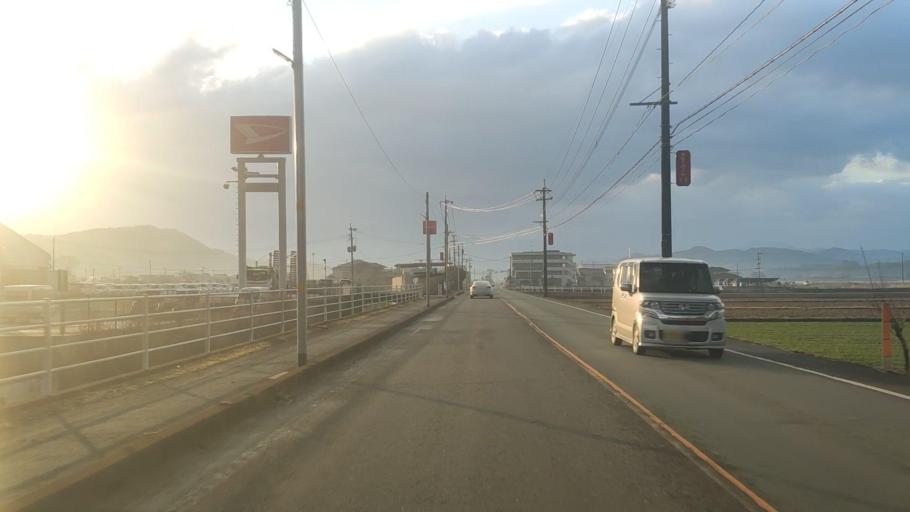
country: JP
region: Kumamoto
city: Uto
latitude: 32.7152
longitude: 130.7731
